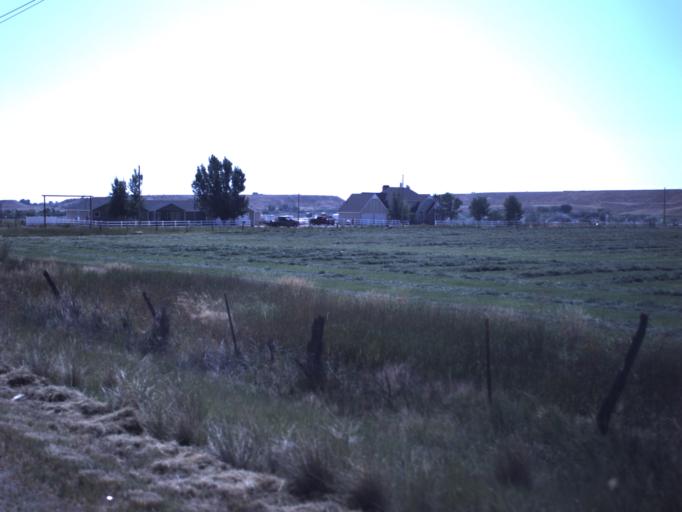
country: US
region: Utah
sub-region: Duchesne County
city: Roosevelt
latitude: 40.2584
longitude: -110.1068
